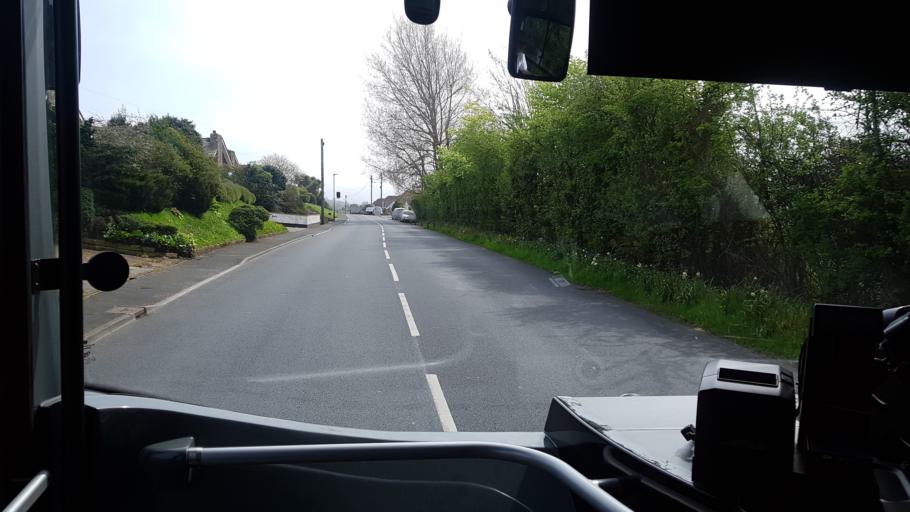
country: GB
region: England
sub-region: Isle of Wight
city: Ventnor
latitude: 50.6223
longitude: -1.2248
